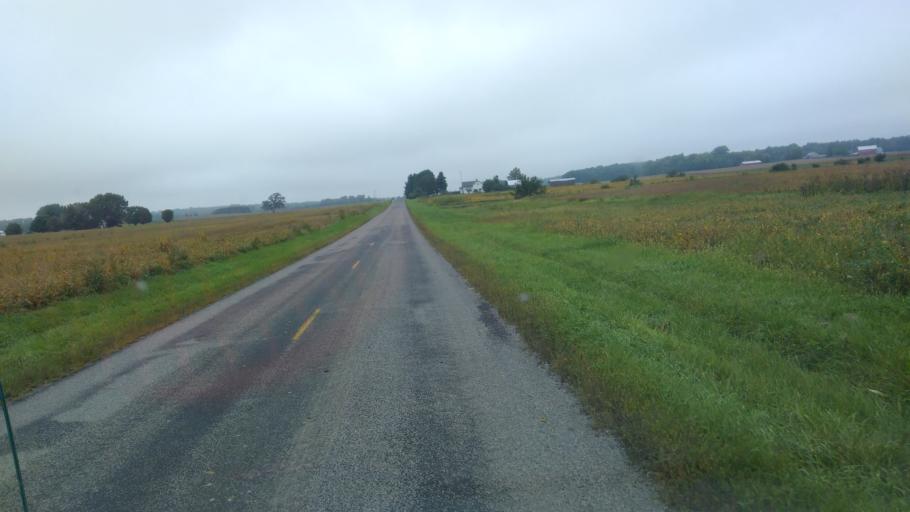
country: US
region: Ohio
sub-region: Hardin County
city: Kenton
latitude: 40.5451
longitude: -83.6343
